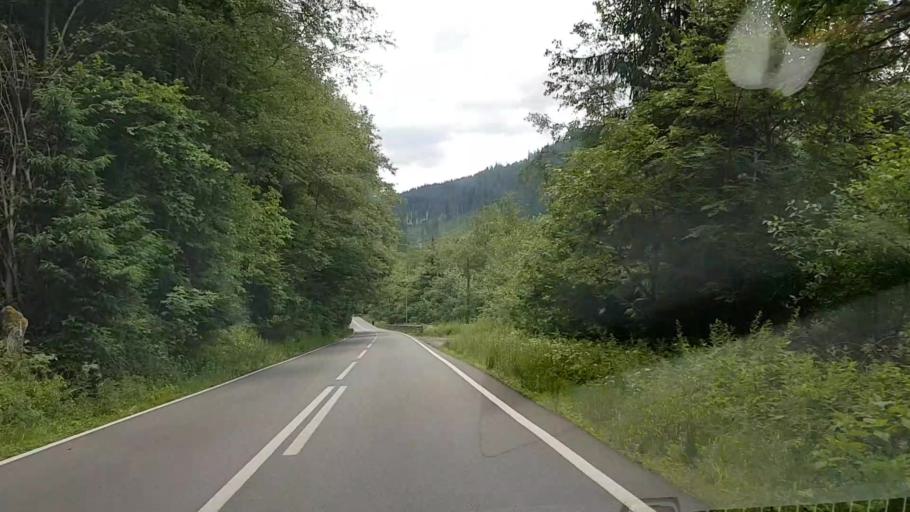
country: RO
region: Suceava
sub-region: Comuna Crucea
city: Crucea
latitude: 47.3683
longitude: 25.5901
